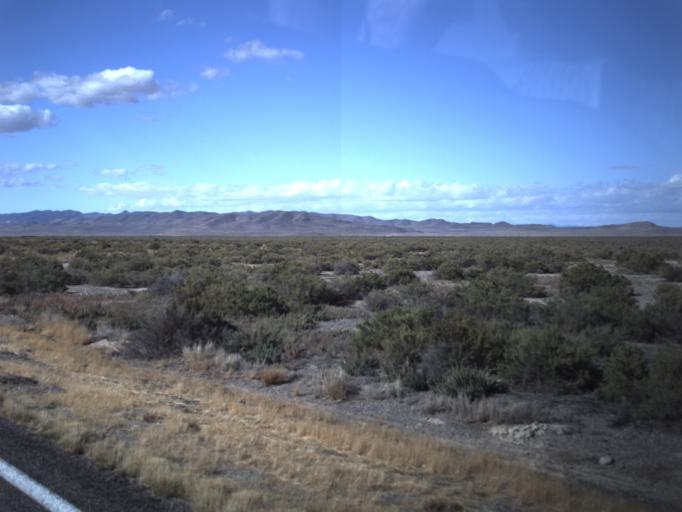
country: US
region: Utah
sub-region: Millard County
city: Delta
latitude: 39.1276
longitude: -112.7335
